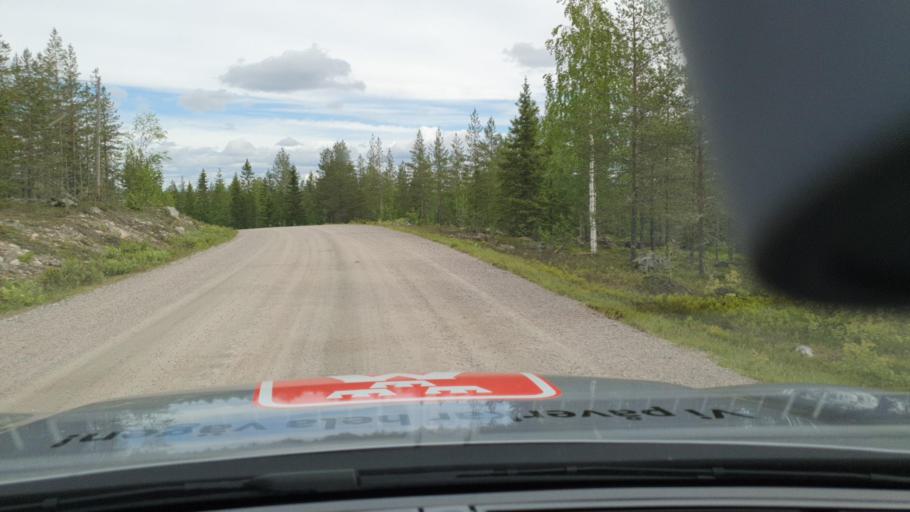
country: SE
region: Norrbotten
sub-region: Kalix Kommun
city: Kalix
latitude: 65.9312
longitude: 23.5259
